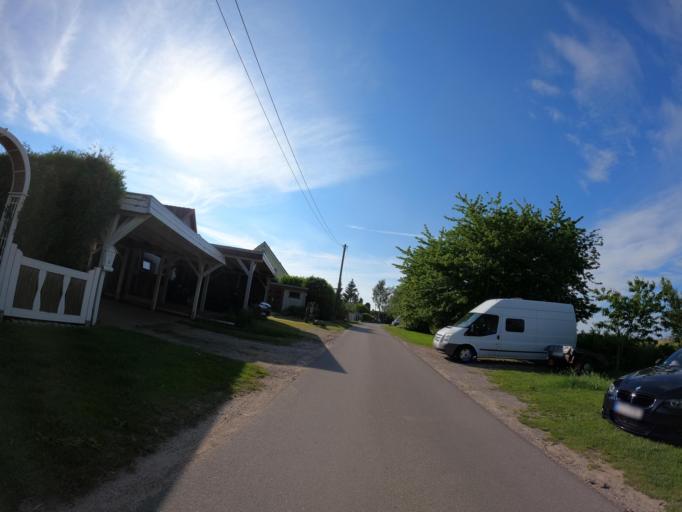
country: DE
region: Mecklenburg-Vorpommern
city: Preetz
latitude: 54.3329
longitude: 12.9725
